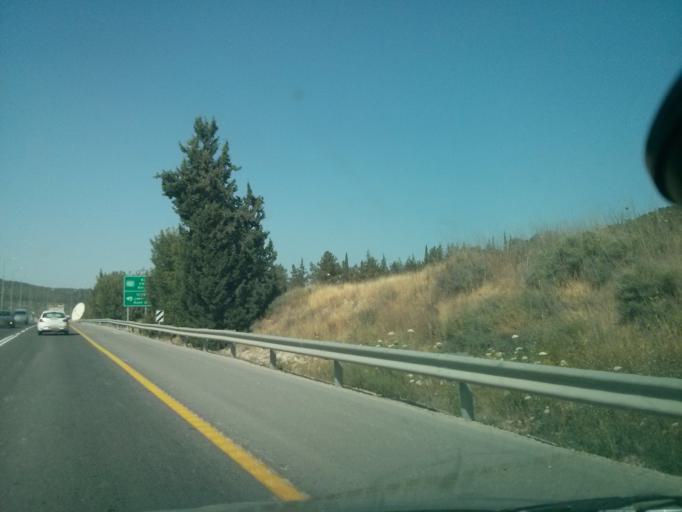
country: IL
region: Jerusalem
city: Bet Shemesh
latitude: 31.6888
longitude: 35.0031
